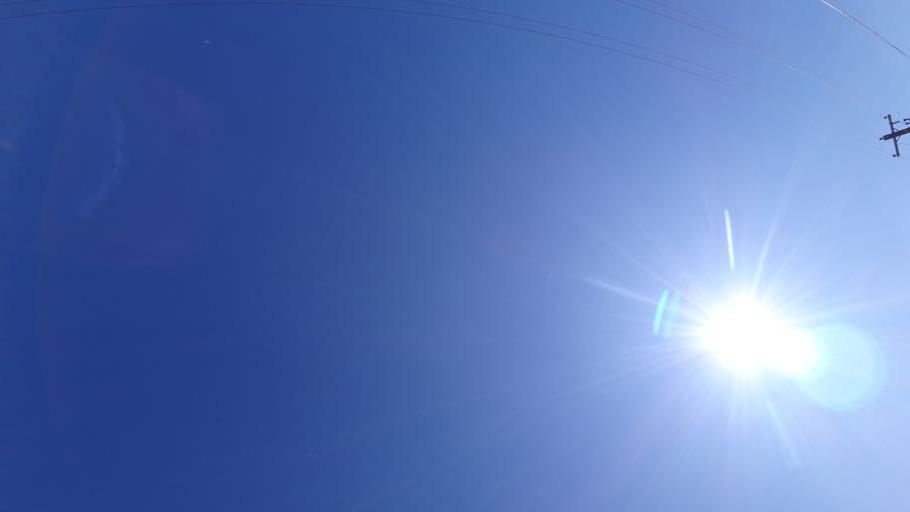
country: US
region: Texas
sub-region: Denton County
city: Lewisville
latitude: 33.0379
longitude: -96.9359
